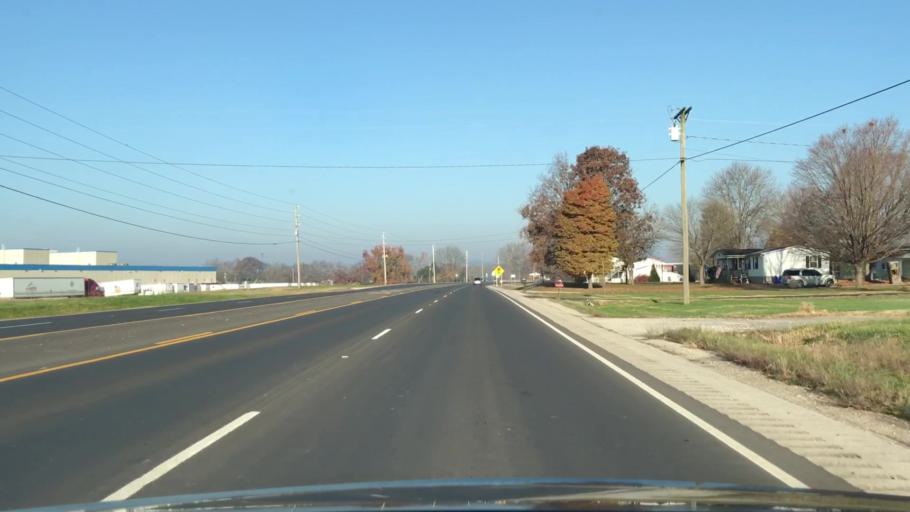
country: US
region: Kentucky
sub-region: Warren County
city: Bowling Green
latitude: 37.0361
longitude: -86.3306
